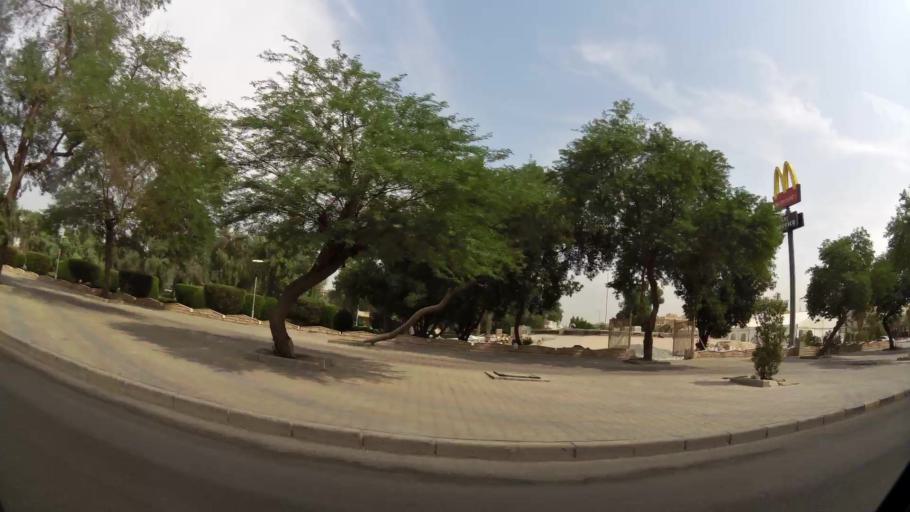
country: KW
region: Al Asimah
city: Ash Shamiyah
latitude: 29.3294
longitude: 47.9900
